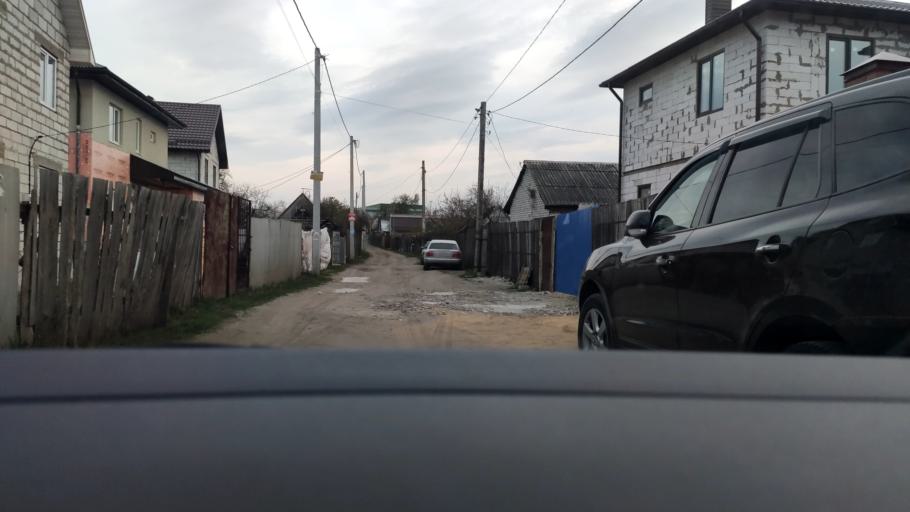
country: RU
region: Voronezj
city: Maslovka
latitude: 51.5996
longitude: 39.2315
